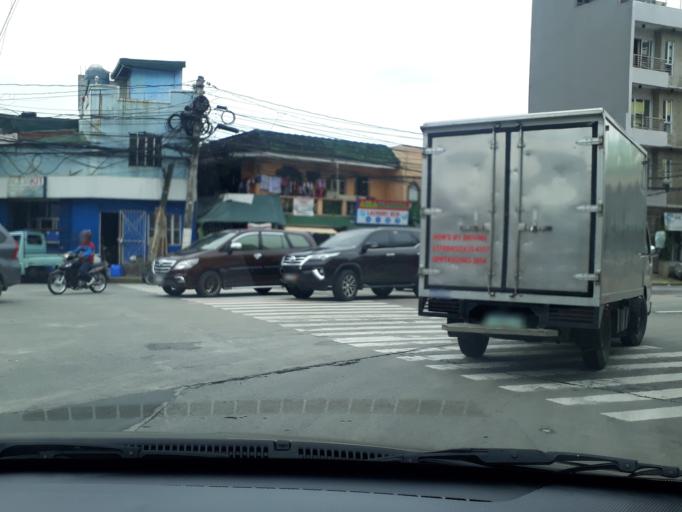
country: PH
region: Metro Manila
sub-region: Mandaluyong
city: Mandaluyong City
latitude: 14.5725
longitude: 121.0291
